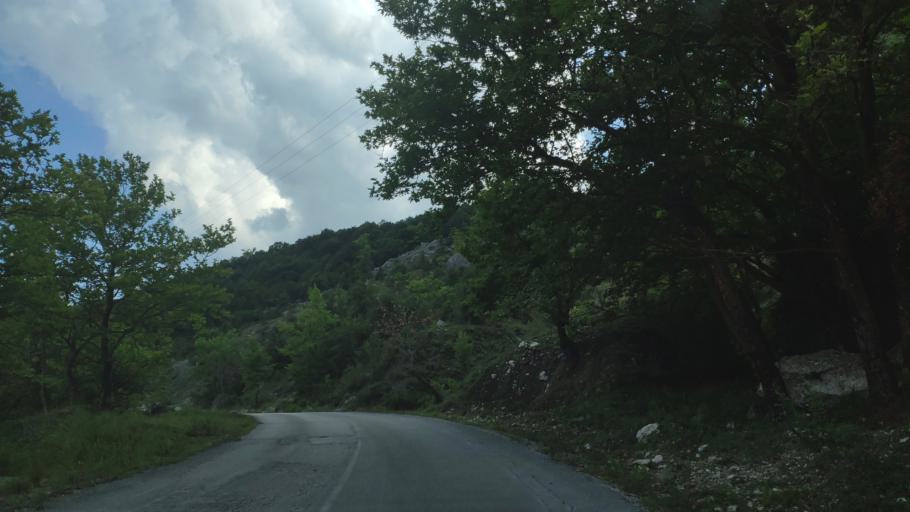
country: GR
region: Epirus
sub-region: Nomos Artas
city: Agios Dimitrios
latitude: 39.4308
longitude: 21.0159
